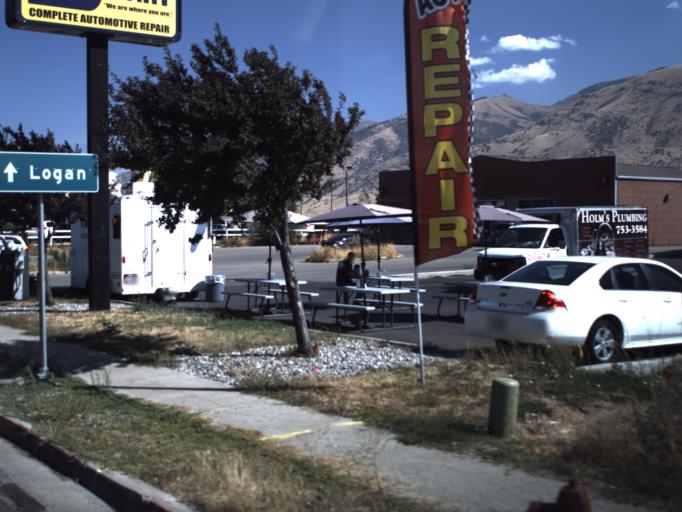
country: US
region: Utah
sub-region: Cache County
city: Hyrum
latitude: 41.6324
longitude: -111.8325
